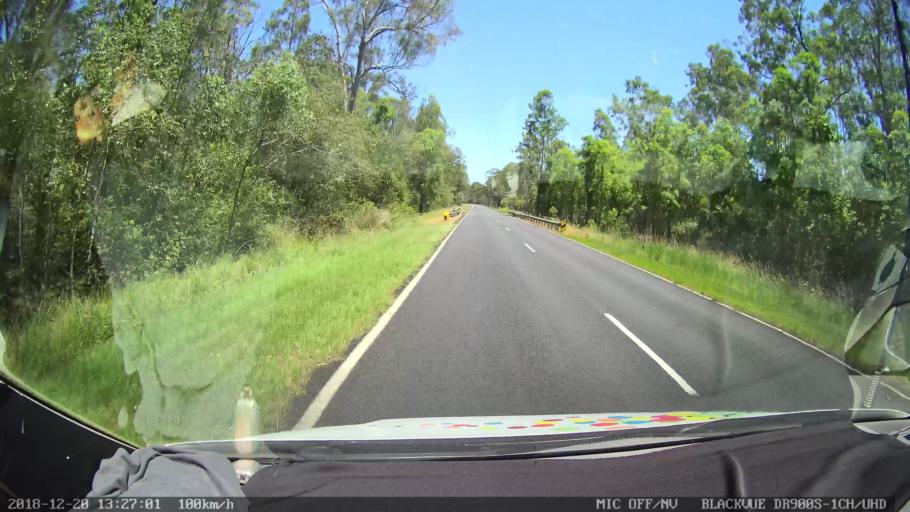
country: AU
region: New South Wales
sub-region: Richmond Valley
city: Casino
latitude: -29.1538
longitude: 152.9932
